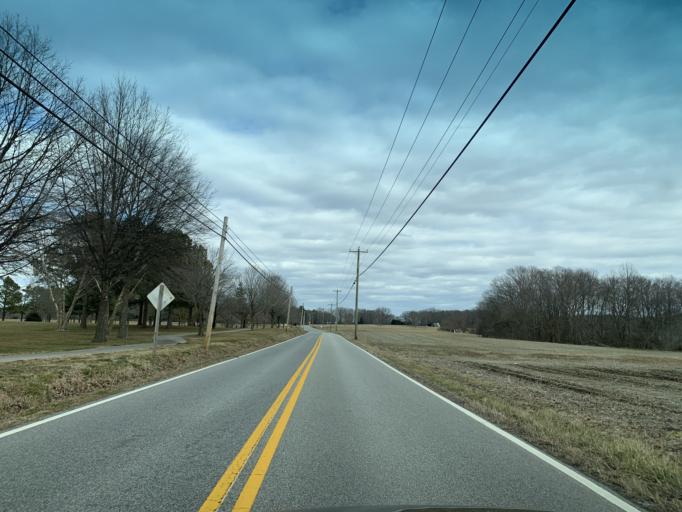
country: US
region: Maryland
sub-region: Queen Anne's County
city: Centreville
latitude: 39.0275
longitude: -76.1083
